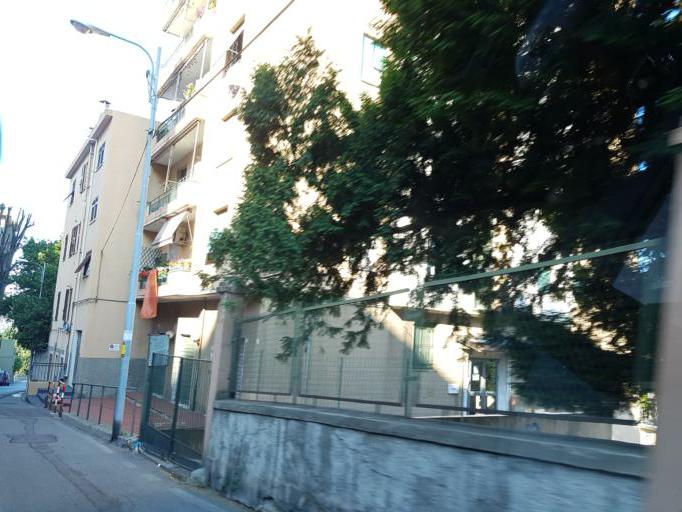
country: IT
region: Liguria
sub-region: Provincia di Genova
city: San Teodoro
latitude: 44.4193
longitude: 8.8755
